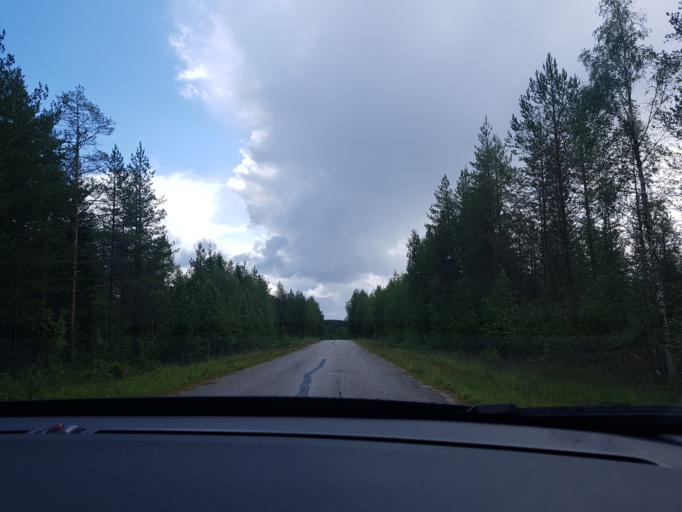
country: FI
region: Kainuu
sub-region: Kehys-Kainuu
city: Kuhmo
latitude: 64.4550
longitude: 29.6548
